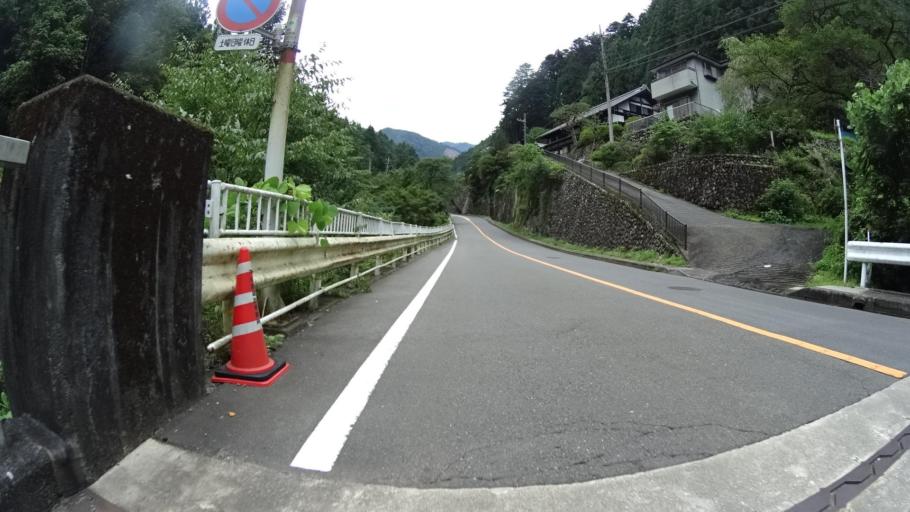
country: JP
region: Yamanashi
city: Uenohara
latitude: 35.7246
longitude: 139.0534
